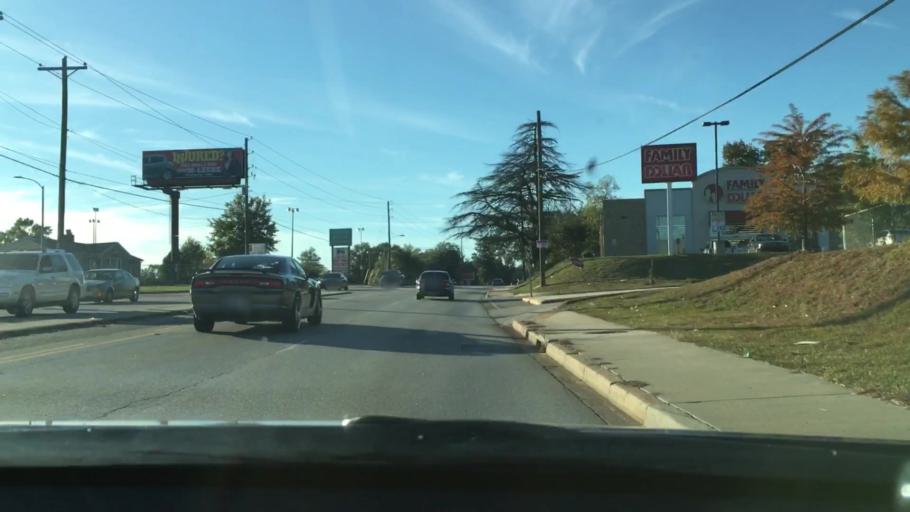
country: US
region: South Carolina
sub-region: Lexington County
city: West Columbia
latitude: 34.0252
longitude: -81.0793
